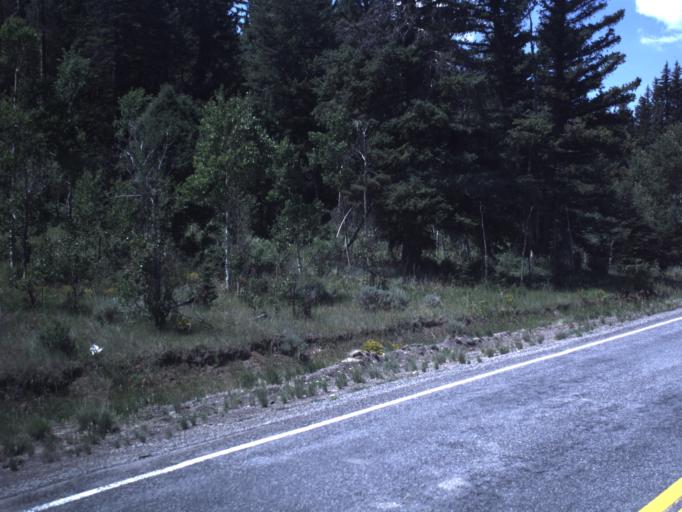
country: US
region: Utah
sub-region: Carbon County
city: Helper
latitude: 39.8586
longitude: -111.1022
